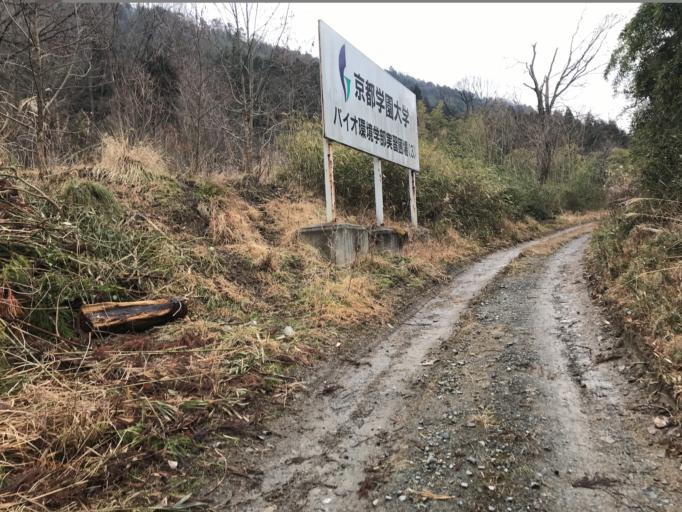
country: JP
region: Kyoto
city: Kameoka
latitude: 34.9894
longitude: 135.5544
